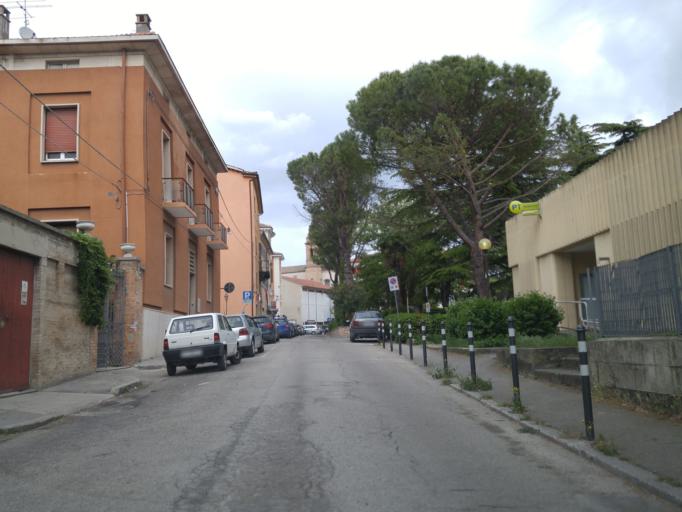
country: IT
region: The Marches
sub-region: Provincia di Pesaro e Urbino
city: Fossombrone
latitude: 43.6882
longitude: 12.8077
